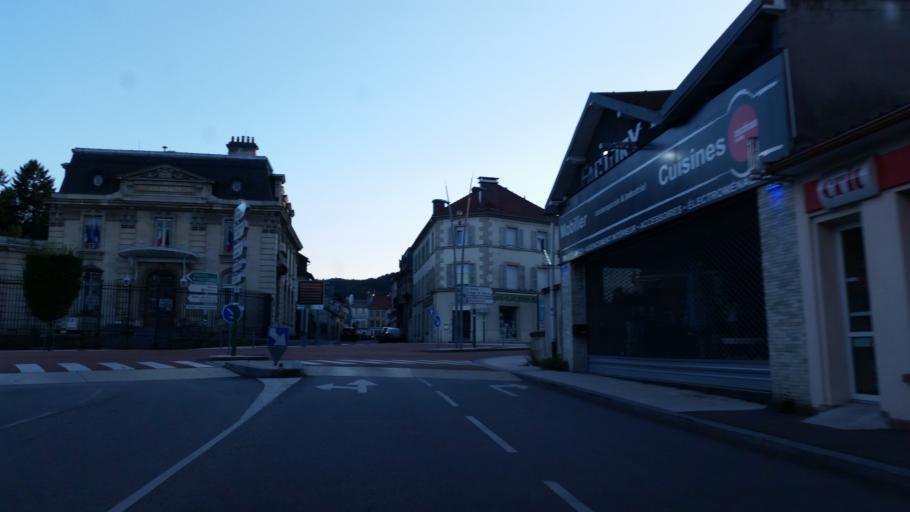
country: FR
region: Lorraine
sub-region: Departement des Vosges
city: Remiremont
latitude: 48.0171
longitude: 6.5962
